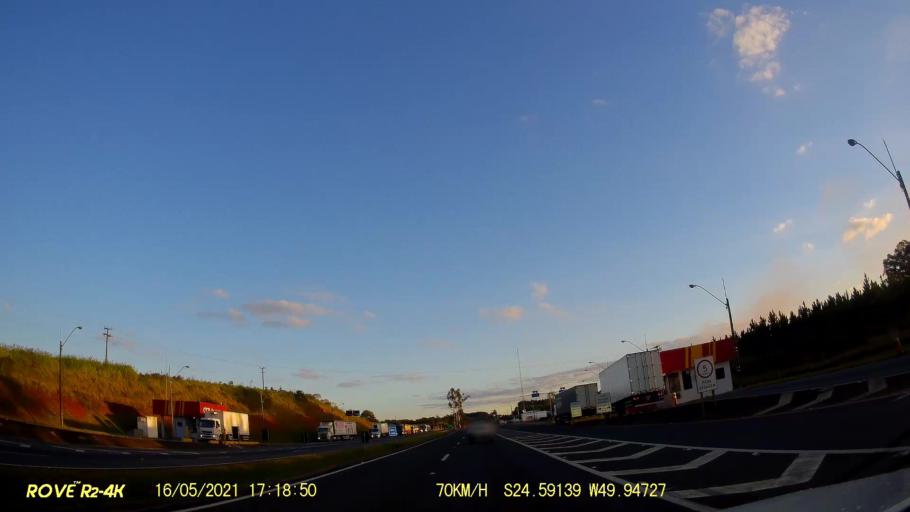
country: BR
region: Parana
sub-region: Pirai Do Sul
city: Pirai do Sul
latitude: -24.5916
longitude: -49.9474
